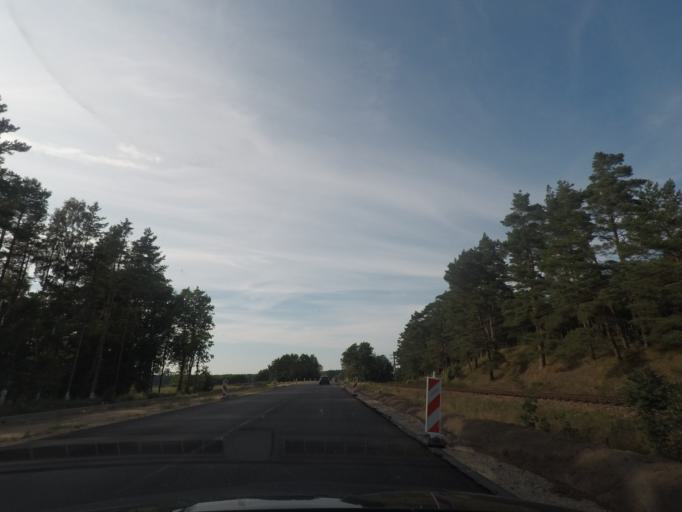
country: PL
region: Pomeranian Voivodeship
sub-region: Powiat leborski
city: Leba
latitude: 54.7241
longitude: 17.5707
